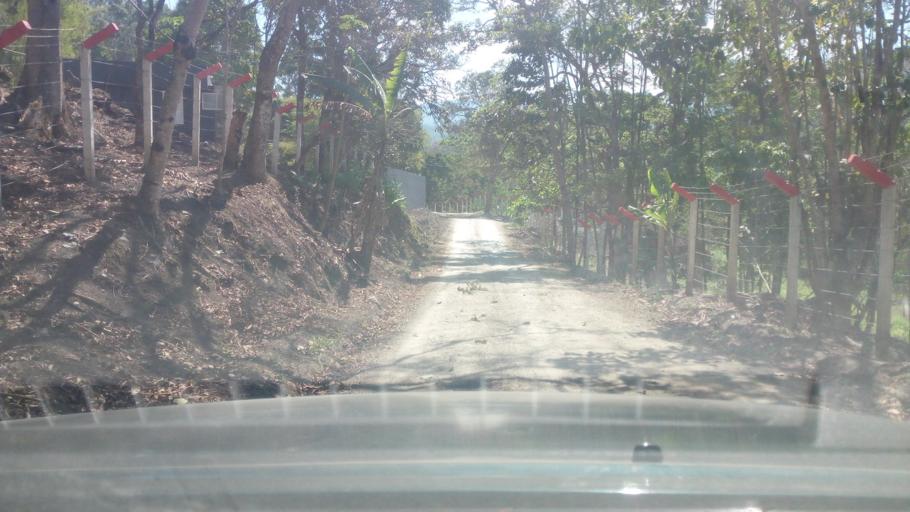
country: CO
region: Boyaca
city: Somondoco
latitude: 4.9859
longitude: -73.4577
